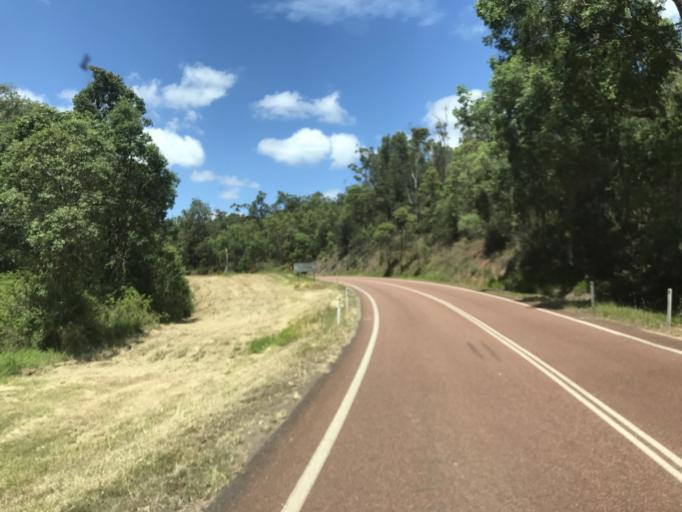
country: AU
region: Queensland
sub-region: Tablelands
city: Ravenshoe
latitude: -17.5974
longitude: 145.4781
